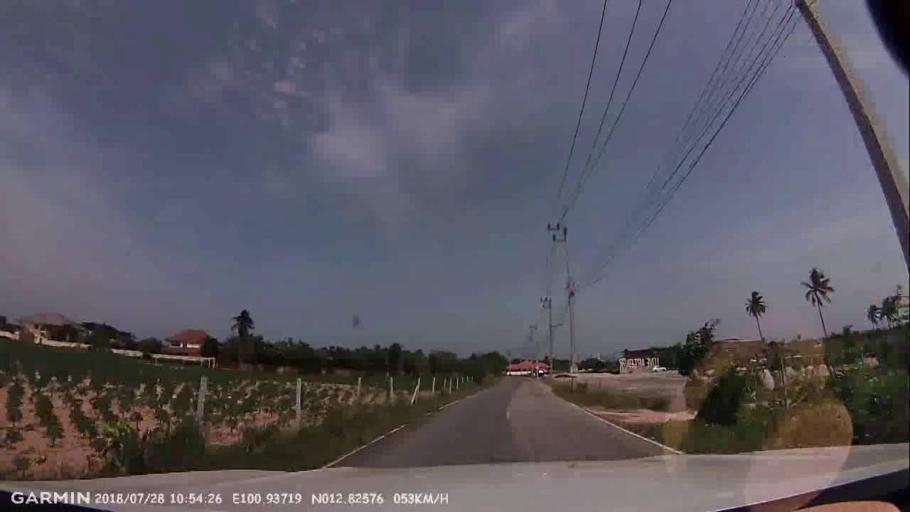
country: TH
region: Chon Buri
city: Phatthaya
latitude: 12.8258
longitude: 100.9370
